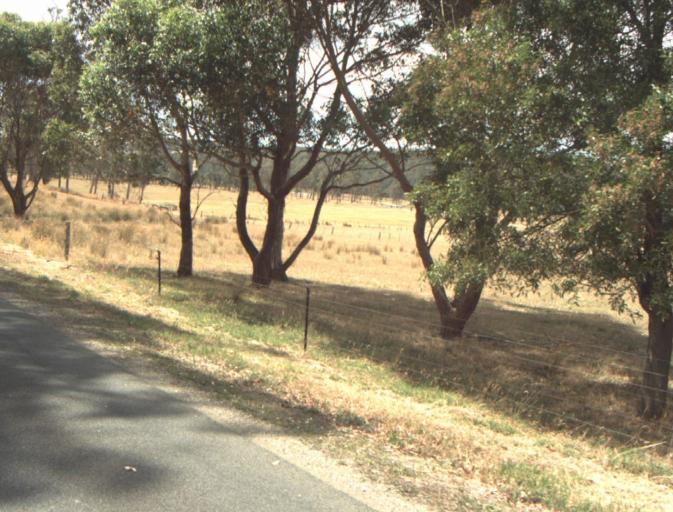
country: AU
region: Tasmania
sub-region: Launceston
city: Mayfield
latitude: -41.2273
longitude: 147.1228
